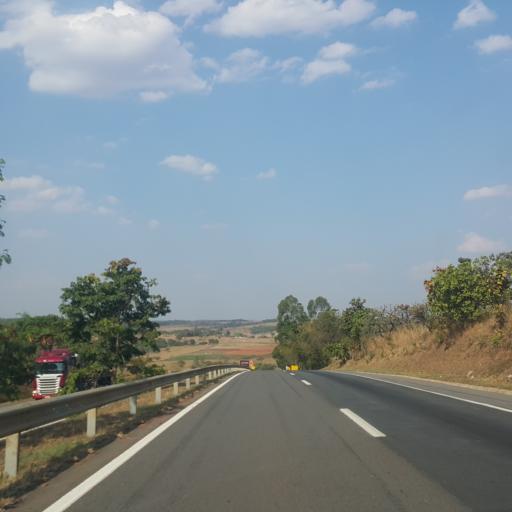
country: BR
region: Goias
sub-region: Abadiania
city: Abadiania
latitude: -16.1105
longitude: -48.5674
